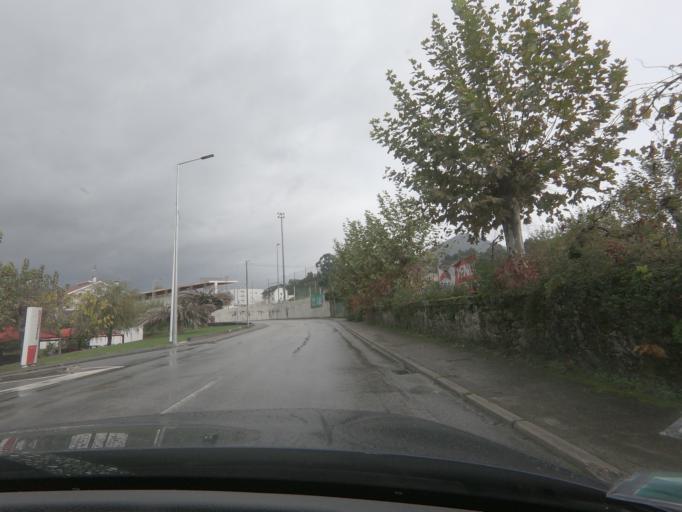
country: PT
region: Vila Real
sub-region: Mondim de Basto
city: Mondim de Basto
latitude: 41.4061
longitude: -7.9565
